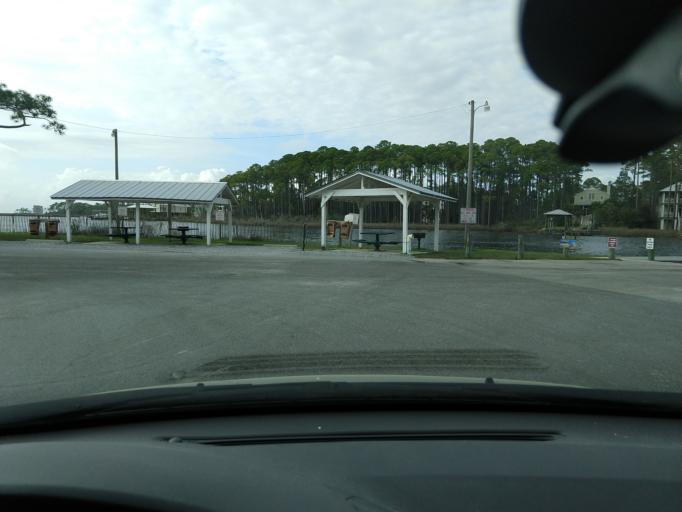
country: US
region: Florida
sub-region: Walton County
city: Seaside
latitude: 30.3986
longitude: -86.2290
